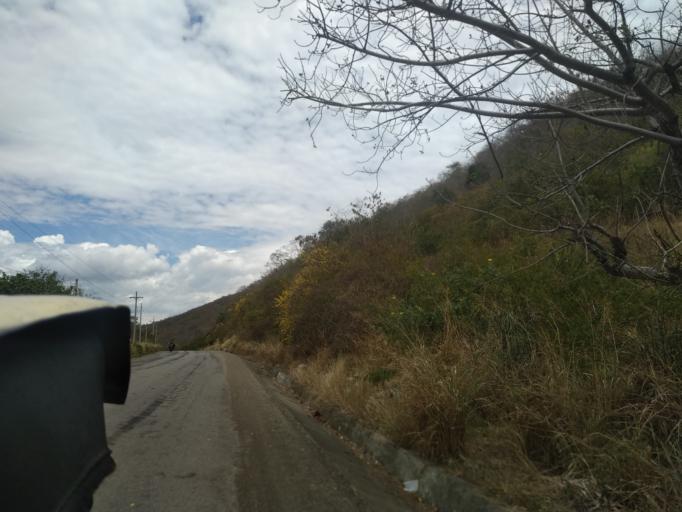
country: PE
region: Cajamarca
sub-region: Provincia de San Ignacio
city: La Coipa
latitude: -5.3985
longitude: -78.7832
